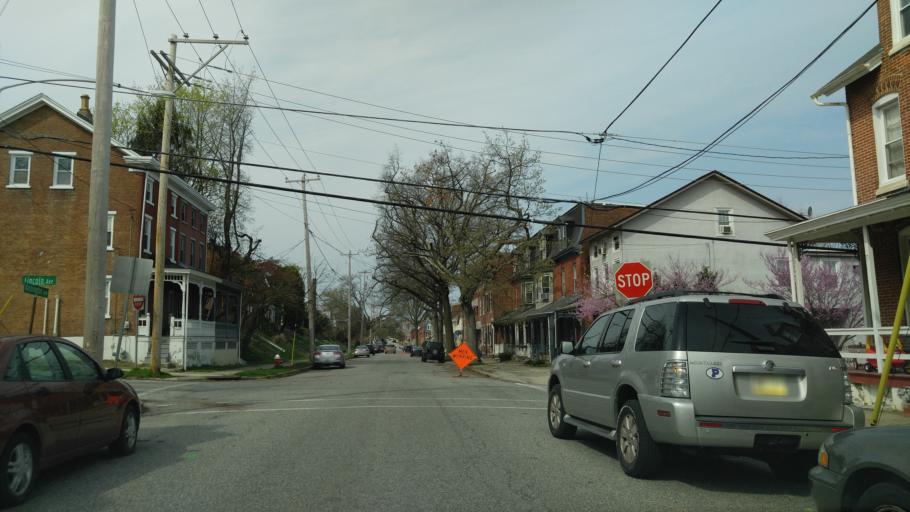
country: US
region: Pennsylvania
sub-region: Chester County
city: Phoenixville
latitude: 40.1297
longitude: -75.5193
